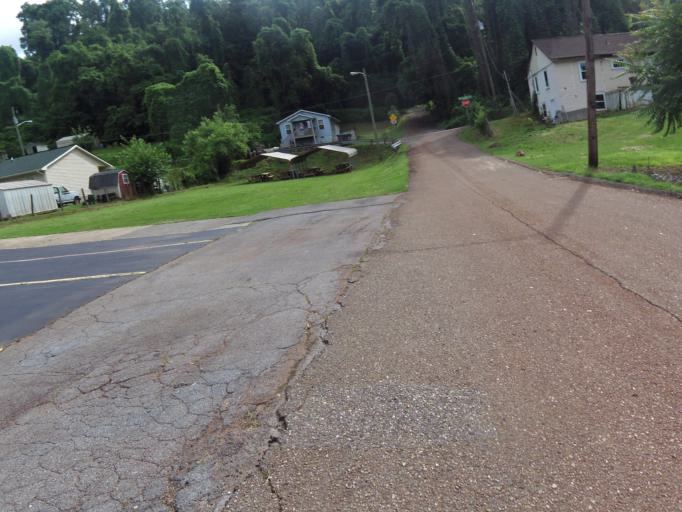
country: US
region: Tennessee
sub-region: Knox County
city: Knoxville
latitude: 35.9538
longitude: -83.9086
